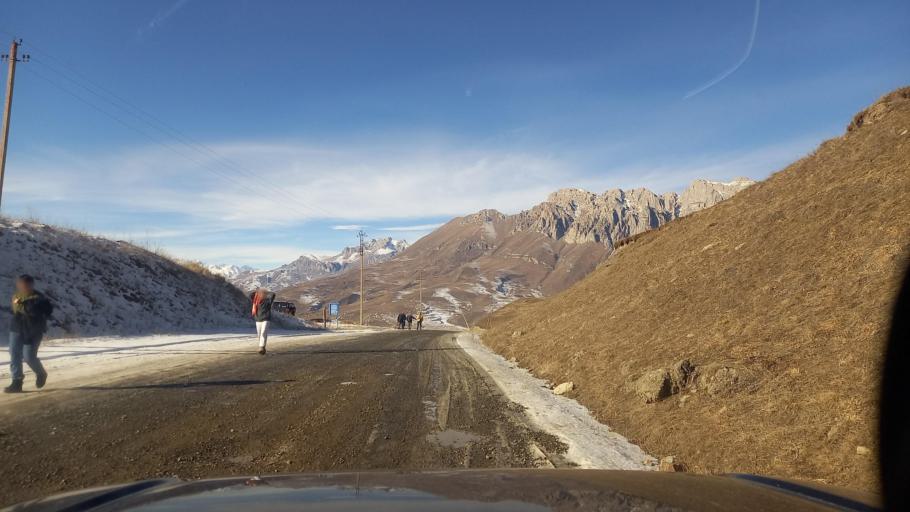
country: RU
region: North Ossetia
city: Verkhniy Fiagdon
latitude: 42.8346
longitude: 44.4789
